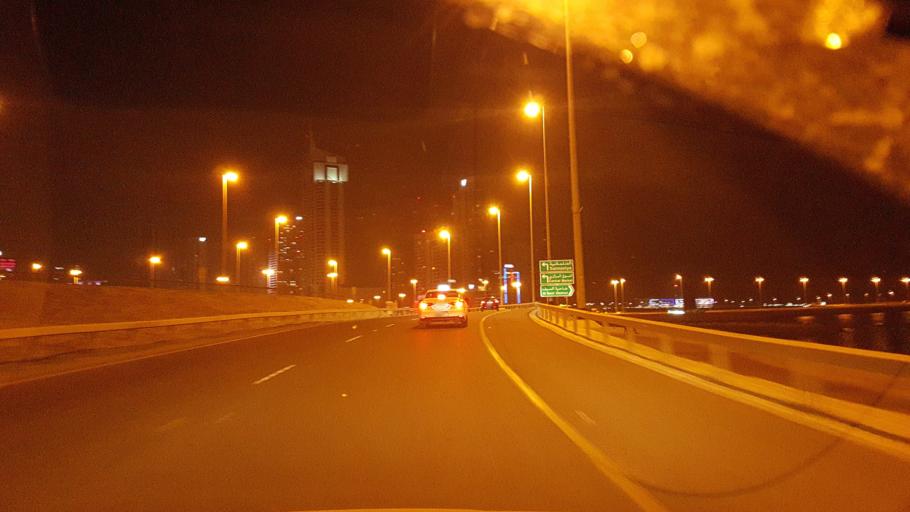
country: BH
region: Manama
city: Jidd Hafs
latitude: 26.2332
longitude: 50.5631
